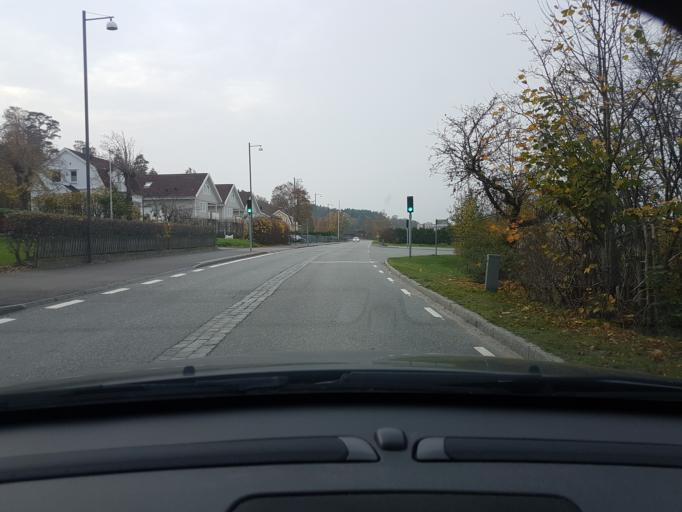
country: SE
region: Vaestra Goetaland
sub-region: Ale Kommun
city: Alvangen
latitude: 57.9565
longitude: 12.1182
